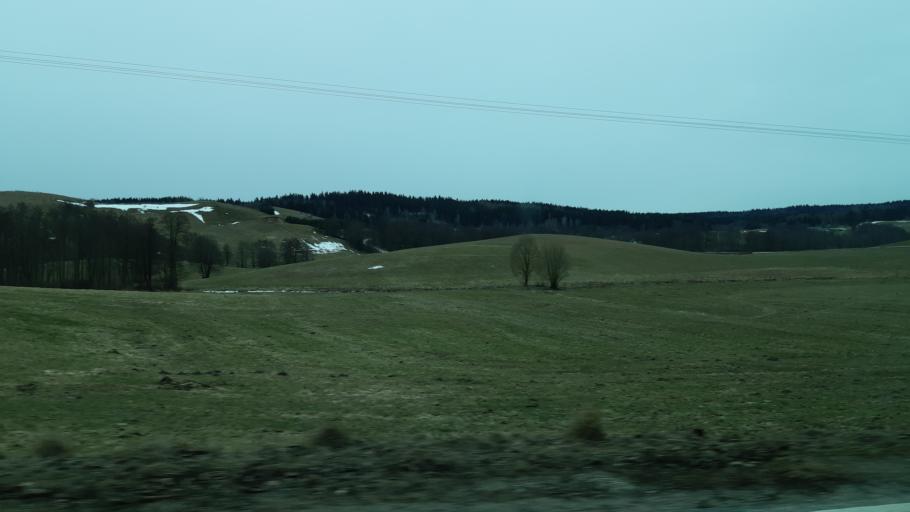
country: PL
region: Podlasie
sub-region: Suwalki
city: Suwalki
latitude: 54.3345
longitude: 22.9322
